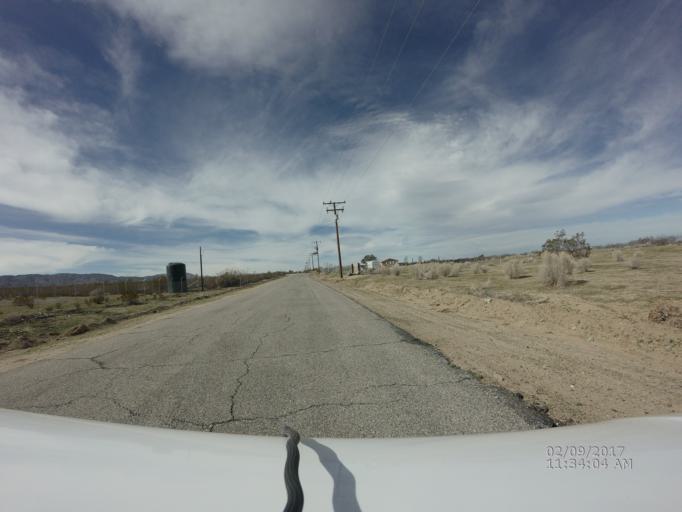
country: US
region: California
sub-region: Los Angeles County
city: Littlerock
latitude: 34.5210
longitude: -117.9257
